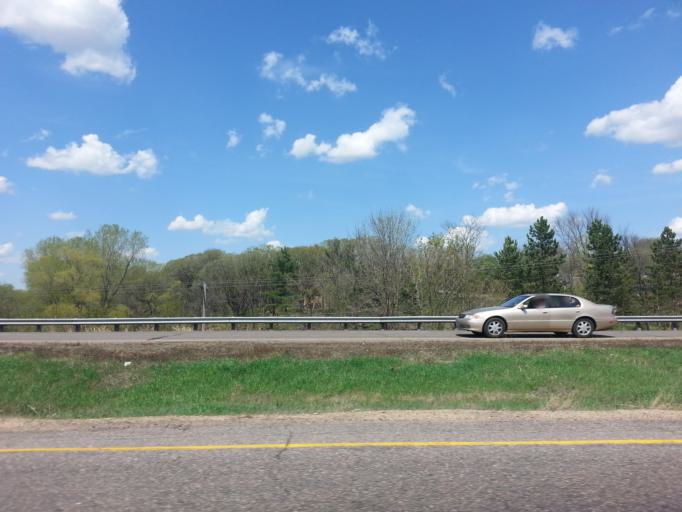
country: US
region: Minnesota
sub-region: Dakota County
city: Mendota Heights
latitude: 44.8837
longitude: -93.1273
